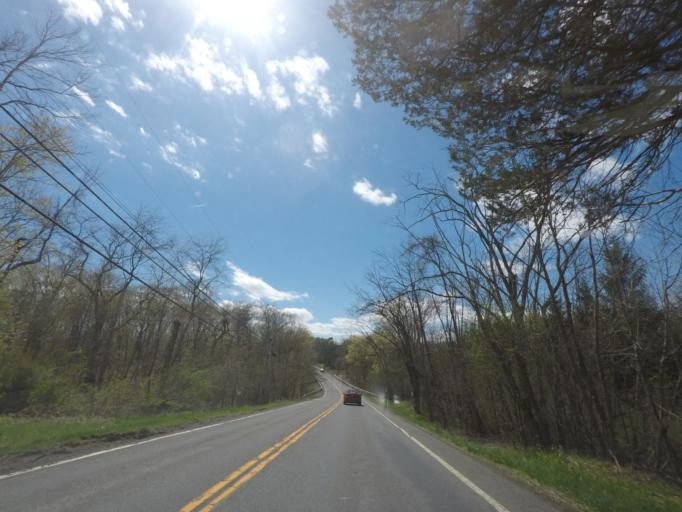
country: US
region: New York
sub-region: Greene County
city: Athens
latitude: 42.2545
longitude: -73.8318
